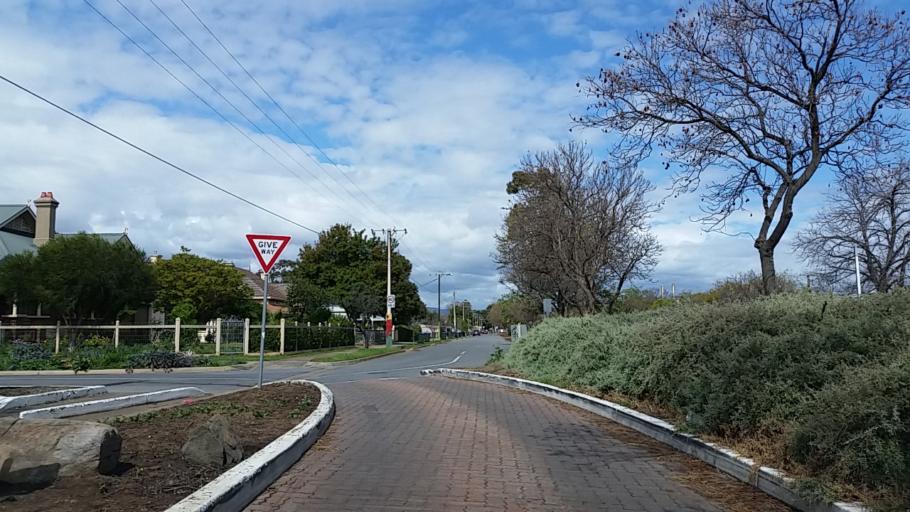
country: AU
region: South Australia
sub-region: Charles Sturt
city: Woodville
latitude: -34.8830
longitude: 138.5458
